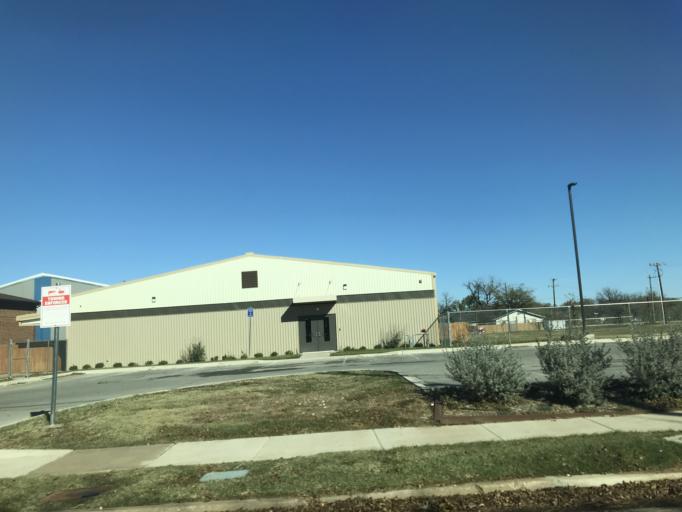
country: US
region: Texas
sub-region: Taylor County
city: Abilene
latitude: 32.4579
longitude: -99.7434
